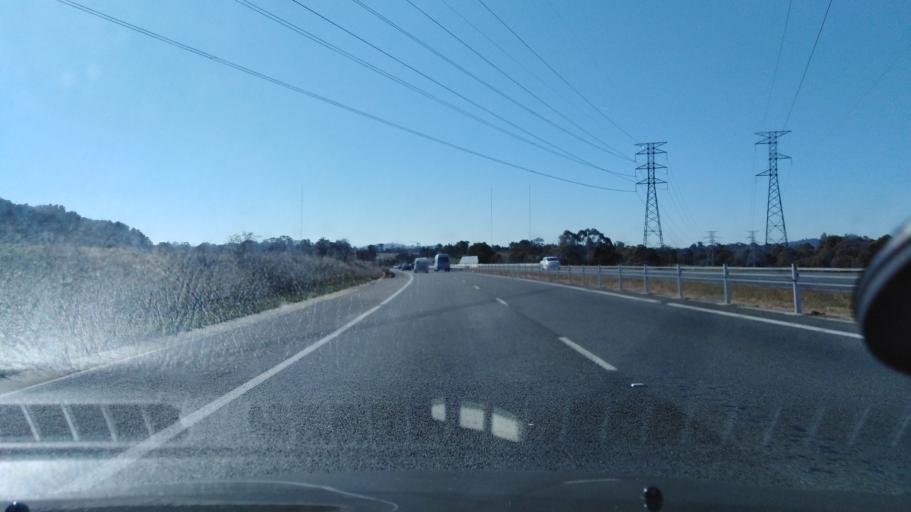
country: AU
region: Australian Capital Territory
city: Kaleen
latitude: -35.2336
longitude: 149.1176
